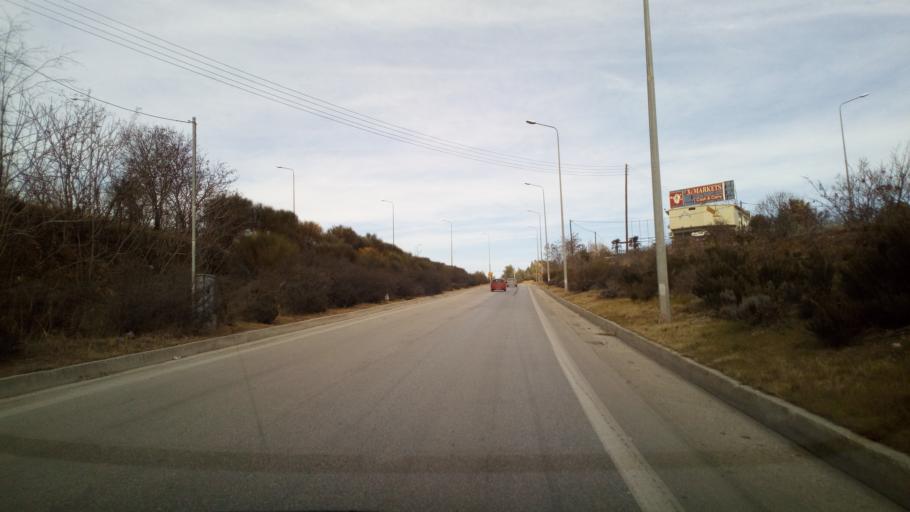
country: GR
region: Central Macedonia
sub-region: Nomos Thessalonikis
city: Efkarpia
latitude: 40.7112
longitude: 22.9587
